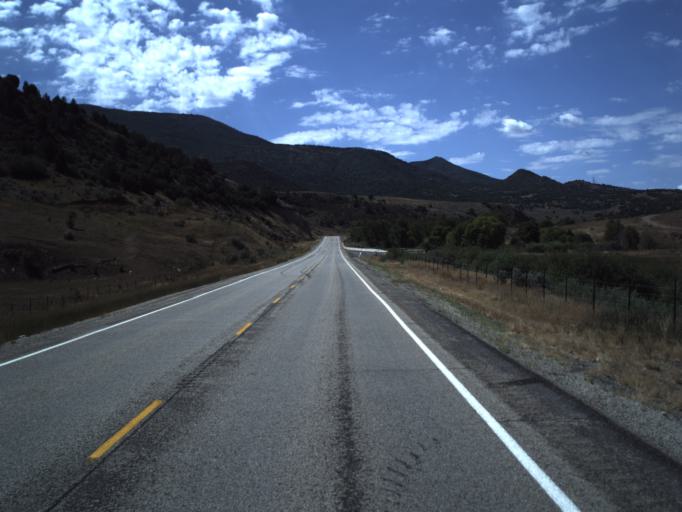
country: US
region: Utah
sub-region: Utah County
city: Woodland Hills
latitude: 39.9815
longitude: -111.5028
